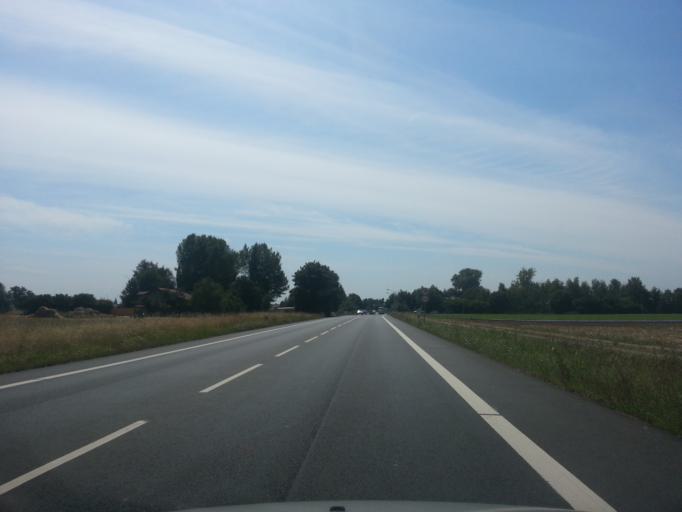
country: DE
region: Hesse
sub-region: Regierungsbezirk Darmstadt
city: Erzhausen
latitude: 49.9256
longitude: 8.6564
